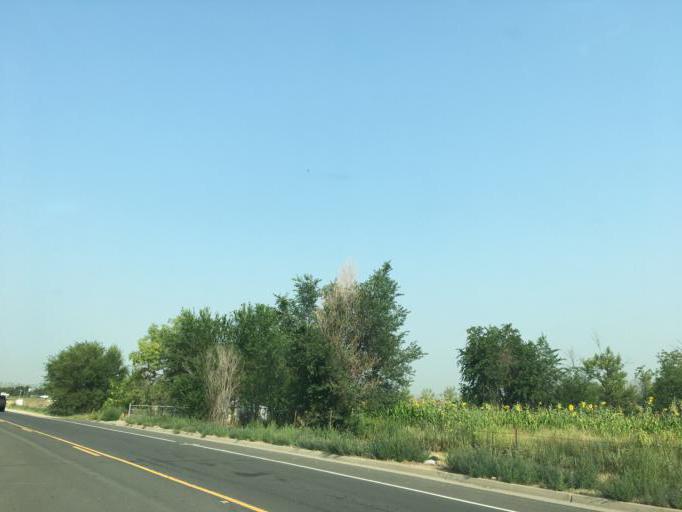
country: US
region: Colorado
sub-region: Adams County
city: Todd Creek
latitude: 39.9143
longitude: -104.8523
